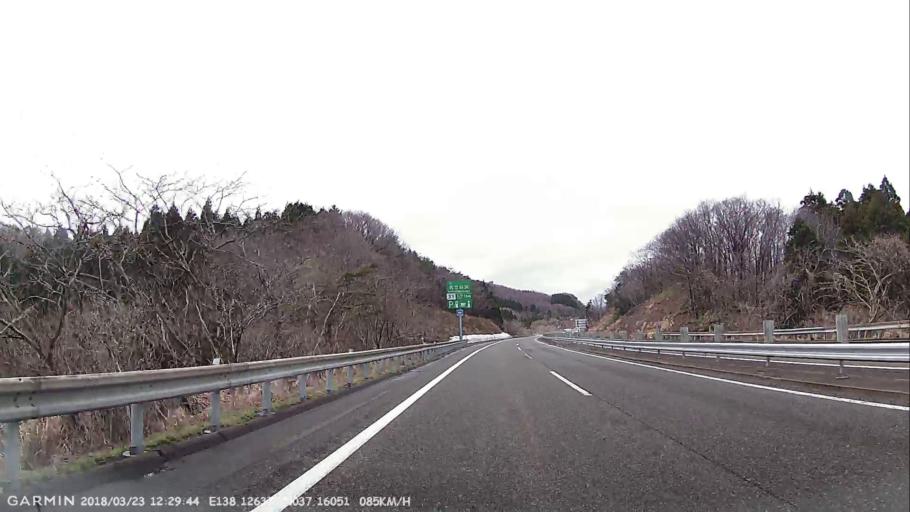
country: JP
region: Niigata
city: Joetsu
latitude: 37.1606
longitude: 138.1262
